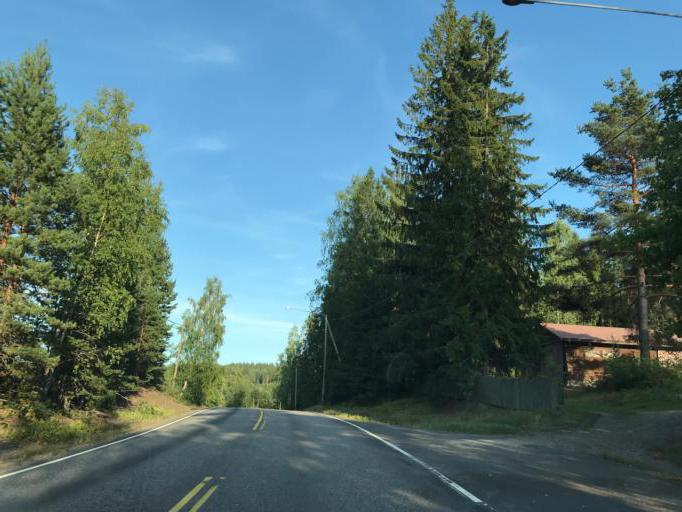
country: FI
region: Uusimaa
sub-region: Helsinki
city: Vihti
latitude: 60.4107
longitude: 24.4421
